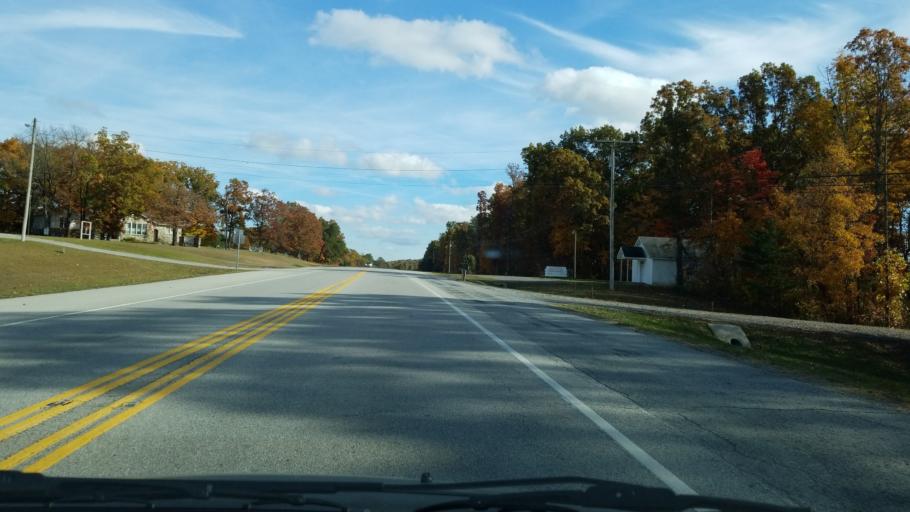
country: US
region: Tennessee
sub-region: Sequatchie County
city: Dunlap
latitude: 35.4735
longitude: -85.4592
